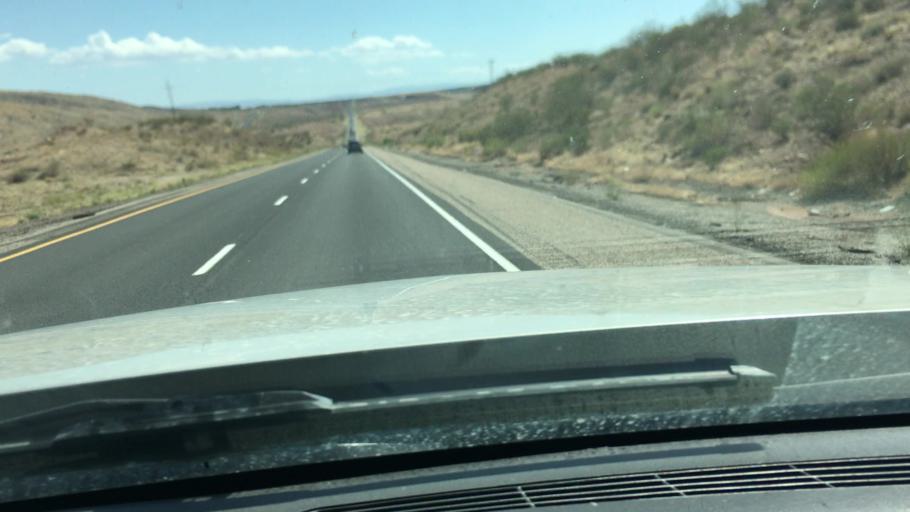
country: US
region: Utah
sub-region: Washington County
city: Hurricane
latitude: 37.2131
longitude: -113.3928
